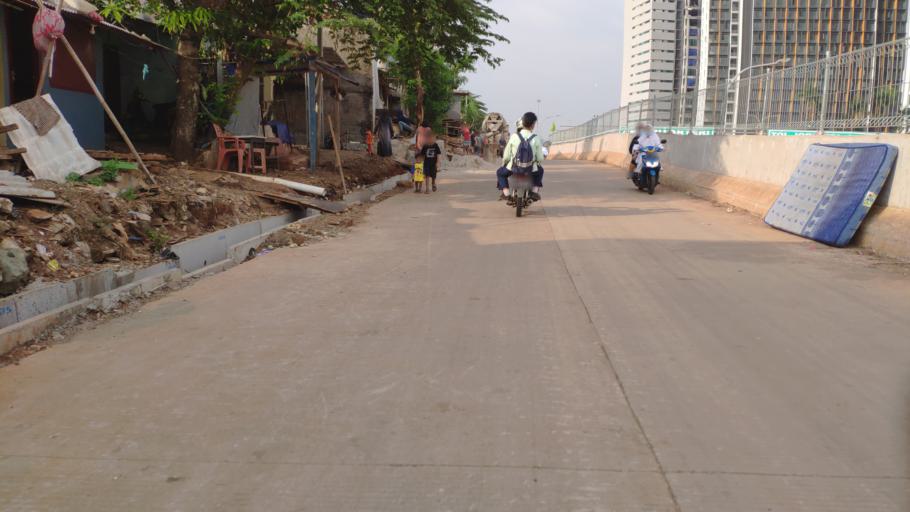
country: ID
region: West Java
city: Pamulang
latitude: -6.2968
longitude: 106.8043
